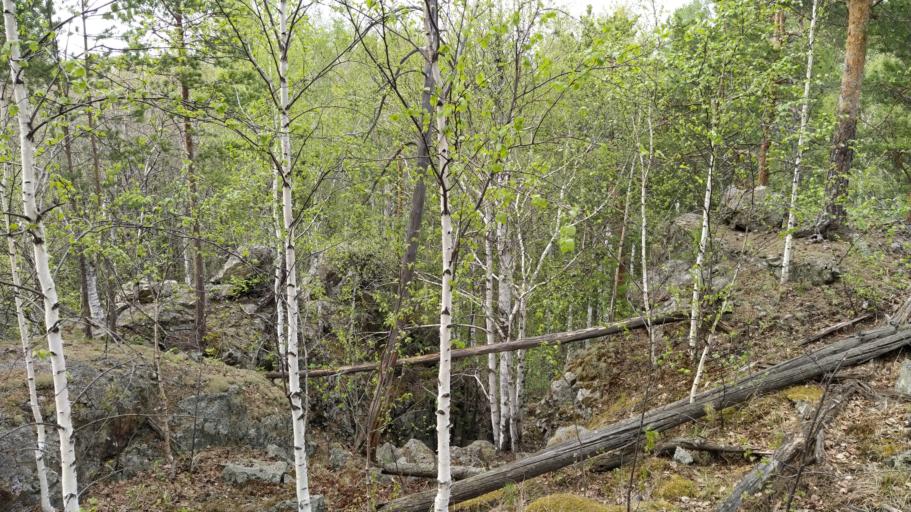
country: RU
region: Sverdlovsk
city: Zyuzel'skiy
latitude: 56.5040
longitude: 60.1013
